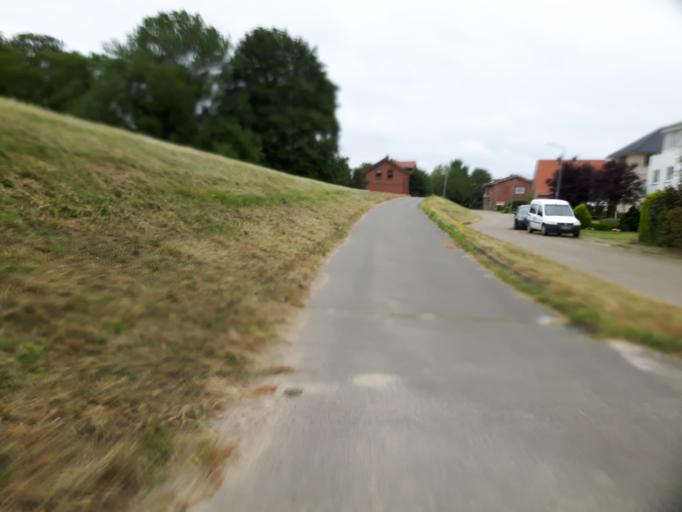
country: DE
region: Lower Saxony
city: Winsen
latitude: 53.3686
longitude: 10.2017
